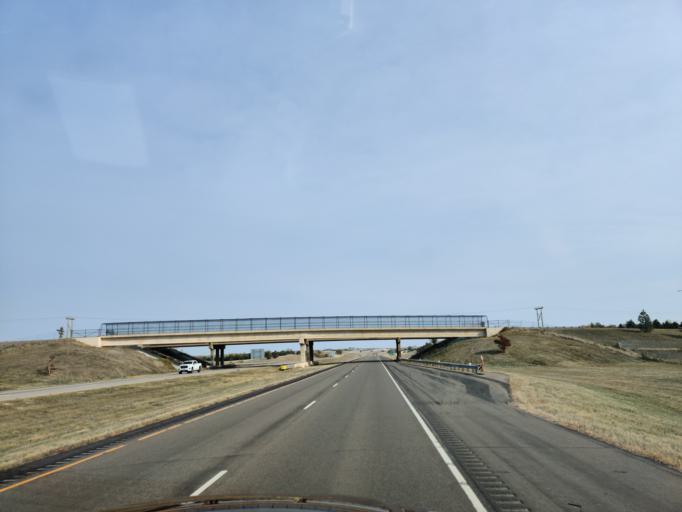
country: US
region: North Dakota
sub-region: Stark County
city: Dickinson
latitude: 46.8947
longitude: -102.7704
